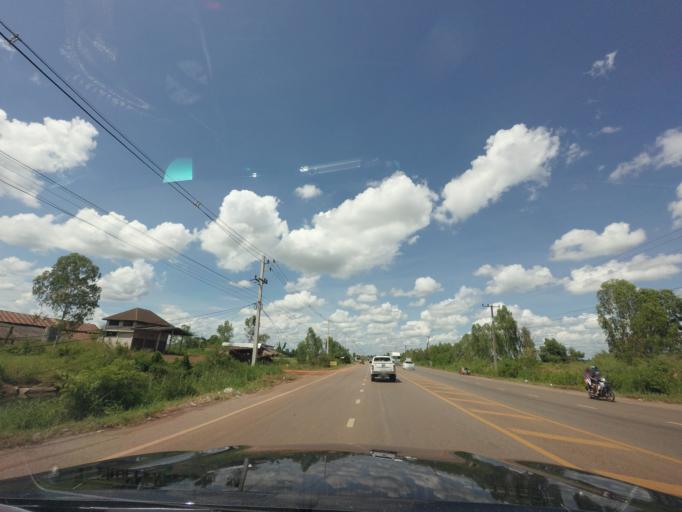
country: TH
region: Changwat Udon Thani
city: Ban Dung
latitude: 17.7157
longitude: 103.2501
